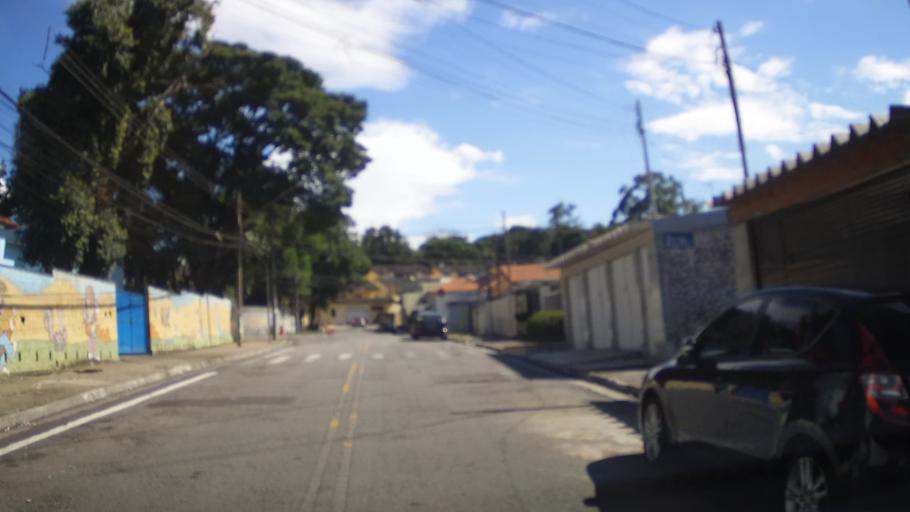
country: BR
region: Sao Paulo
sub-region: Guarulhos
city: Guarulhos
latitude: -23.4564
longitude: -46.5462
